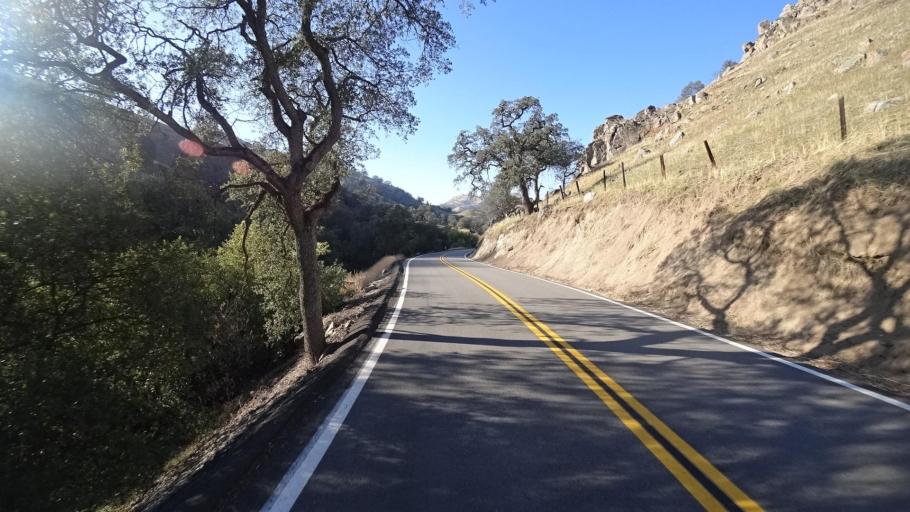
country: US
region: California
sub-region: Kern County
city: Alta Sierra
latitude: 35.7093
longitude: -118.8242
